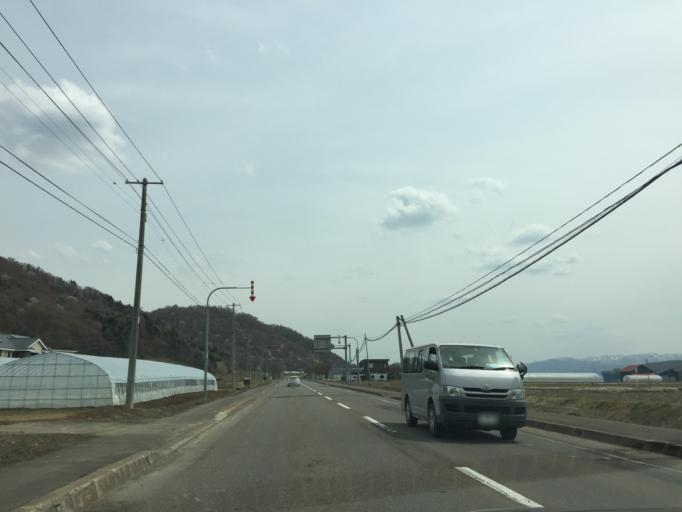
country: JP
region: Hokkaido
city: Ashibetsu
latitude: 43.5426
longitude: 142.1597
